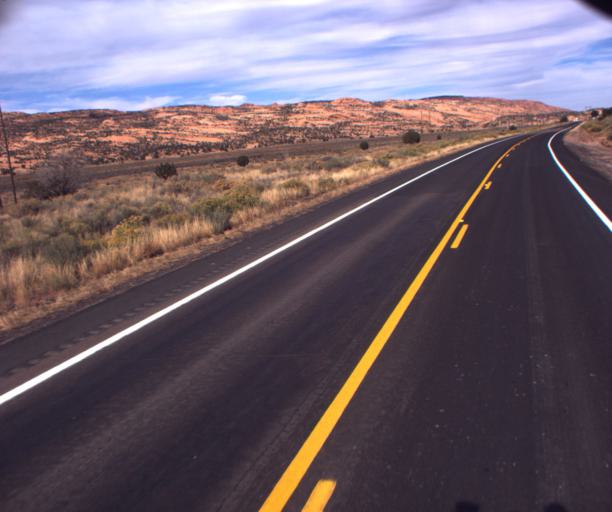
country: US
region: Arizona
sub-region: Navajo County
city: Kayenta
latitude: 36.6137
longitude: -110.4708
